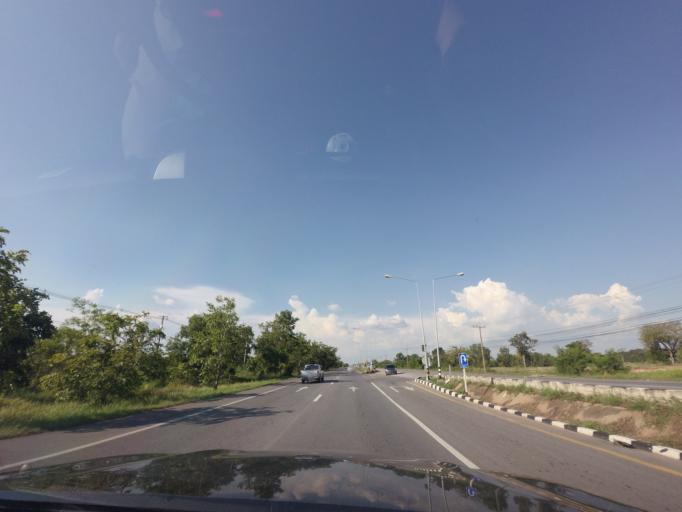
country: TH
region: Khon Kaen
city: Non Sila
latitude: 15.9834
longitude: 102.6966
